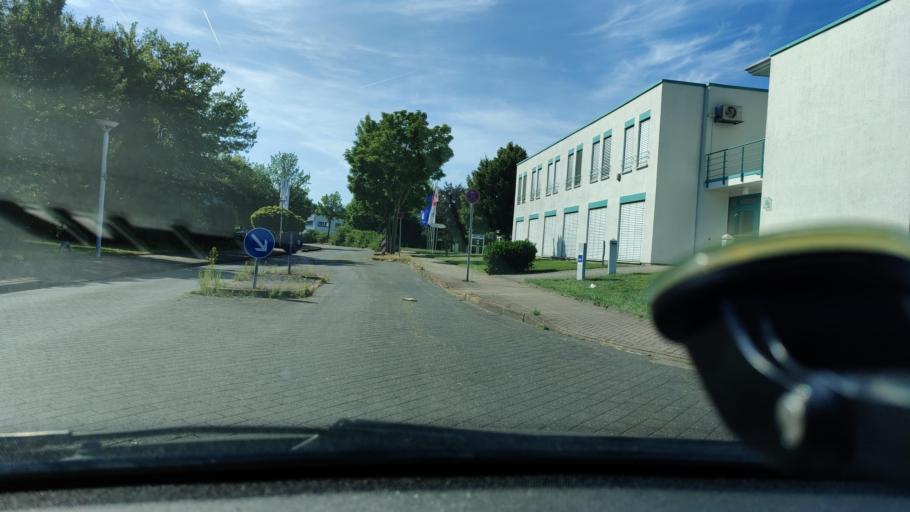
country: DE
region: North Rhine-Westphalia
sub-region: Regierungsbezirk Dusseldorf
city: Kamp-Lintfort
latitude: 51.4838
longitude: 6.5362
